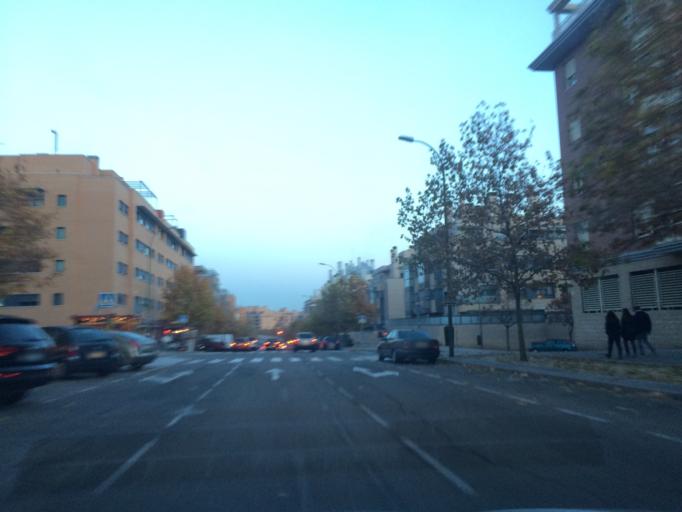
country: ES
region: Madrid
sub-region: Provincia de Madrid
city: Fuencarral-El Pardo
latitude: 40.5034
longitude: -3.7053
